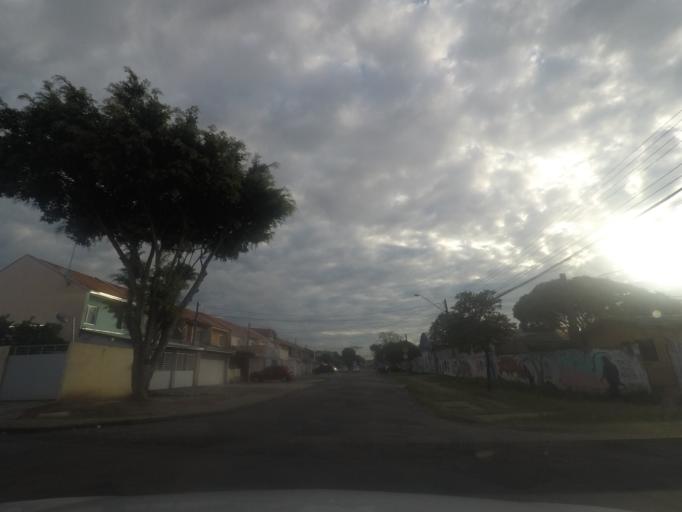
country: BR
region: Parana
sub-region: Pinhais
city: Pinhais
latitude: -25.4654
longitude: -49.2043
